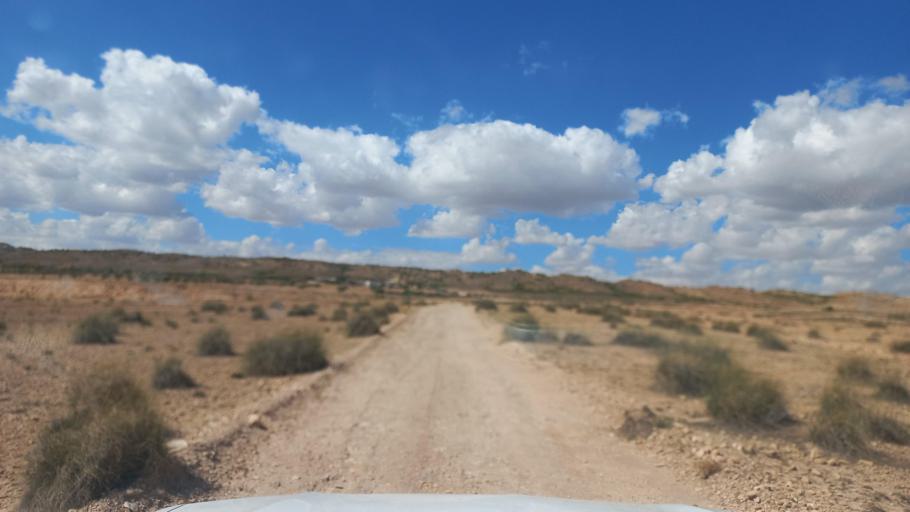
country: TN
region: Al Qasrayn
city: Sbiba
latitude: 35.3617
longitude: 9.0029
